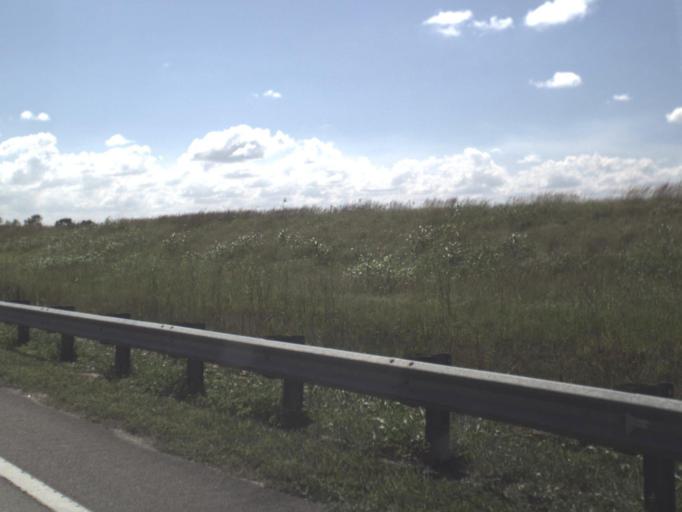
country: US
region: Florida
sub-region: Glades County
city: Moore Haven
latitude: 26.8735
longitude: -81.1227
